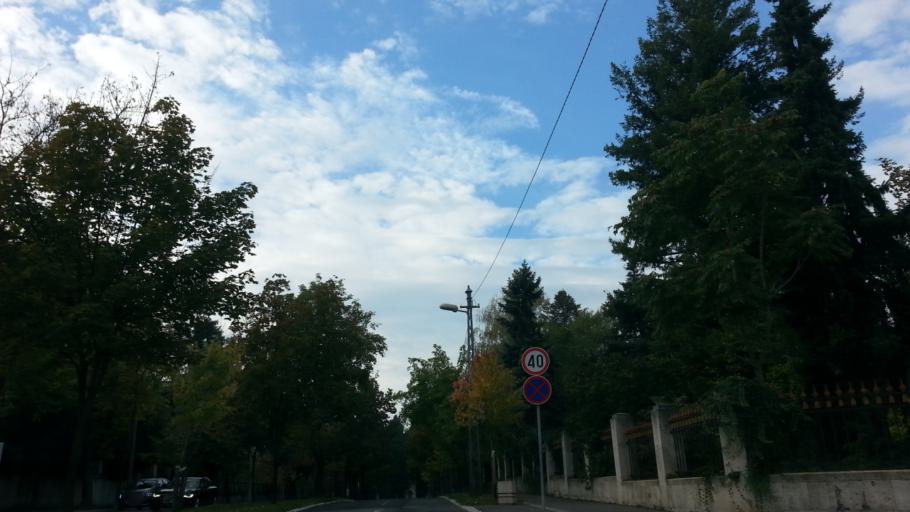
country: RS
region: Central Serbia
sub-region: Belgrade
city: Savski Venac
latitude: 44.7717
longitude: 20.4543
